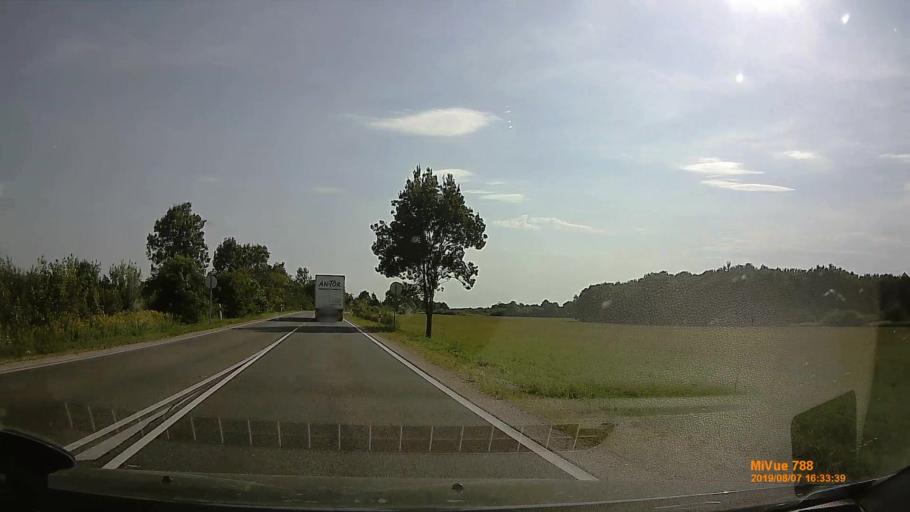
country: HU
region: Zala
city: Lenti
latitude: 46.6316
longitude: 16.4747
